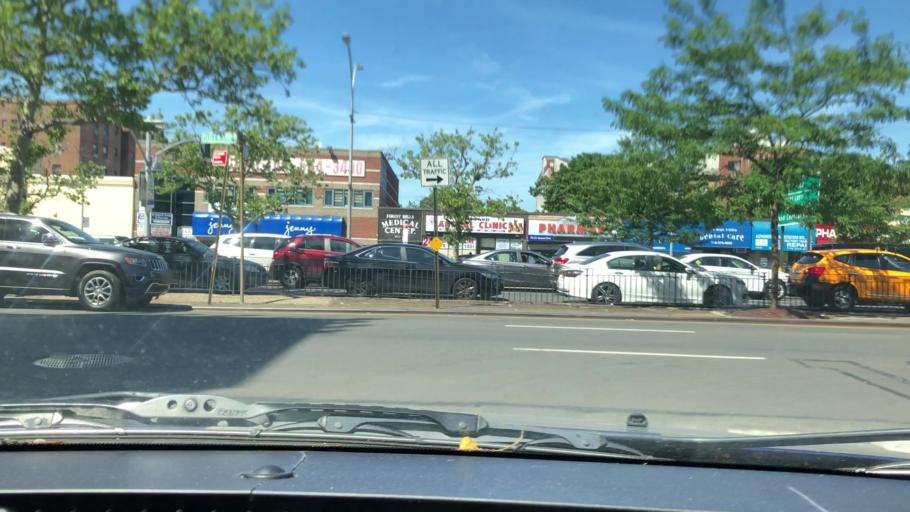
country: US
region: New York
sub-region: Queens County
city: Borough of Queens
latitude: 40.7175
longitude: -73.8361
